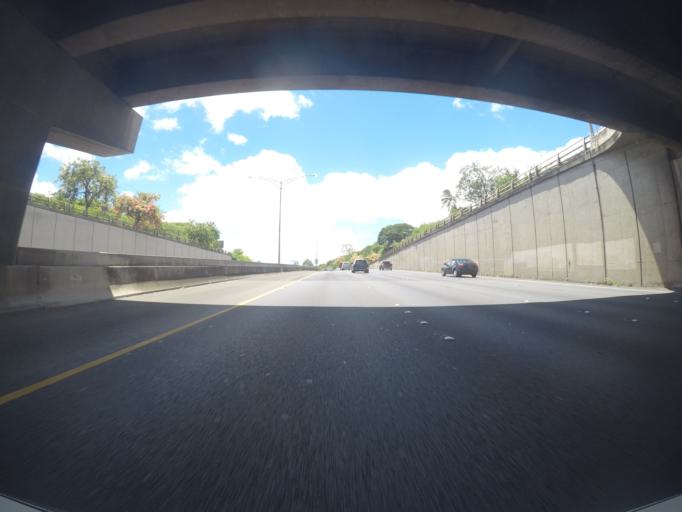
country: US
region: Hawaii
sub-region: Honolulu County
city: Halawa Heights
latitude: 21.3669
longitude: -157.9046
